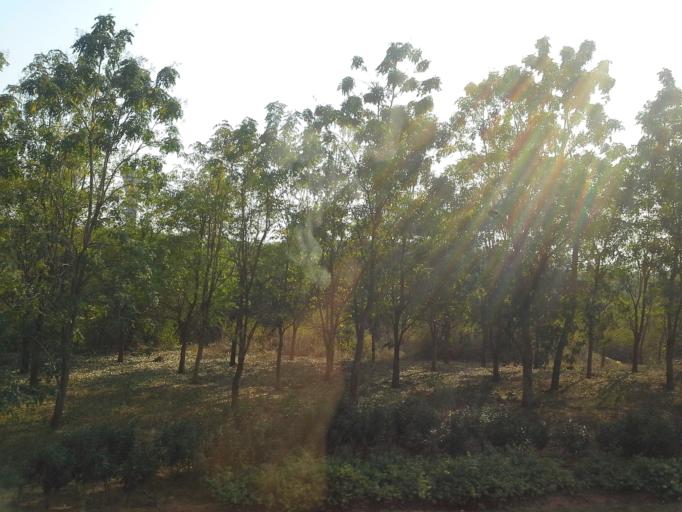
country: IN
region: Telangana
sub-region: Rangareddi
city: Balapur
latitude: 17.2406
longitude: 78.4213
